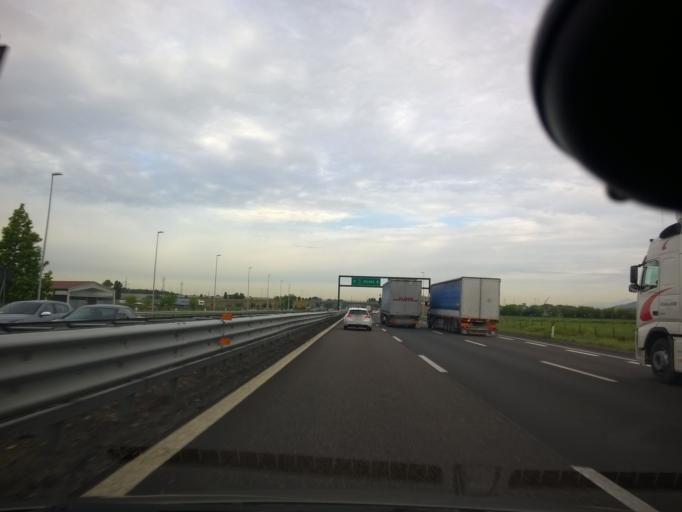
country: IT
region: Lombardy
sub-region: Provincia di Brescia
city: Rezzato
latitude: 45.4809
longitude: 10.3286
